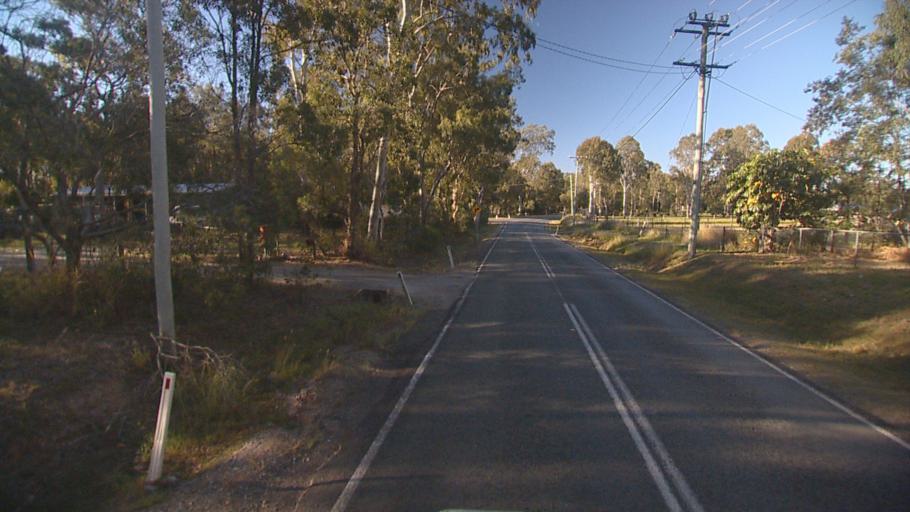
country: AU
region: Queensland
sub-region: Logan
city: Chambers Flat
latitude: -27.7507
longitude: 153.0546
